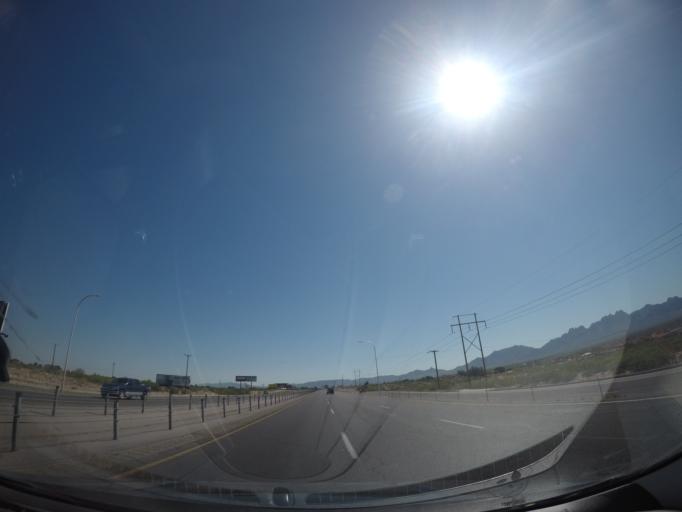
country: US
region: New Mexico
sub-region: Dona Ana County
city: Las Cruces
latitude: 32.3743
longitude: -106.7377
